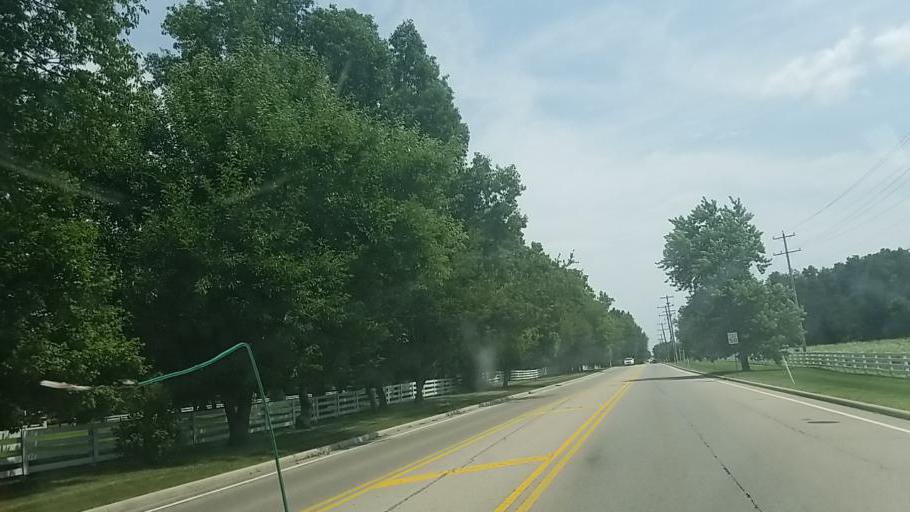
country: US
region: Ohio
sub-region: Franklin County
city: New Albany
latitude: 40.0542
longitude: -82.8381
